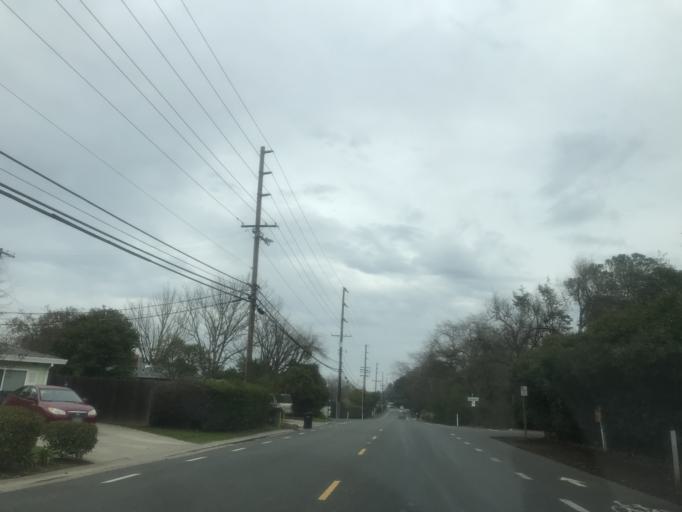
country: US
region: California
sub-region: Sacramento County
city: Arden-Arcade
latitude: 38.5812
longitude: -121.3875
